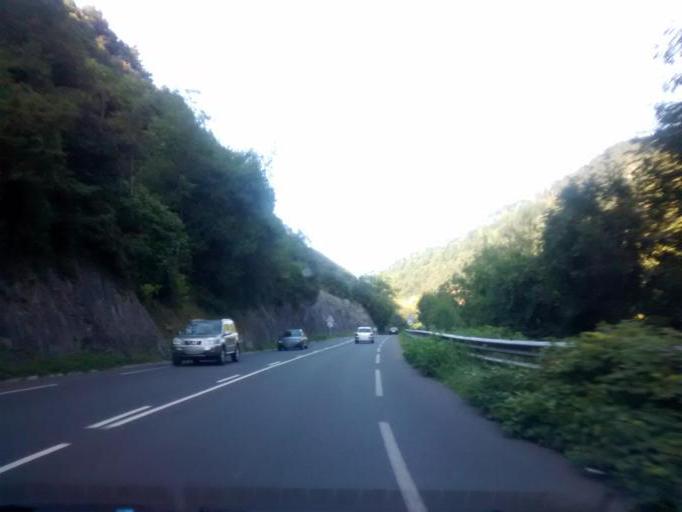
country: ES
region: Basque Country
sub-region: Provincia de Guipuzcoa
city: Mendaro
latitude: 43.2613
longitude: -2.3797
